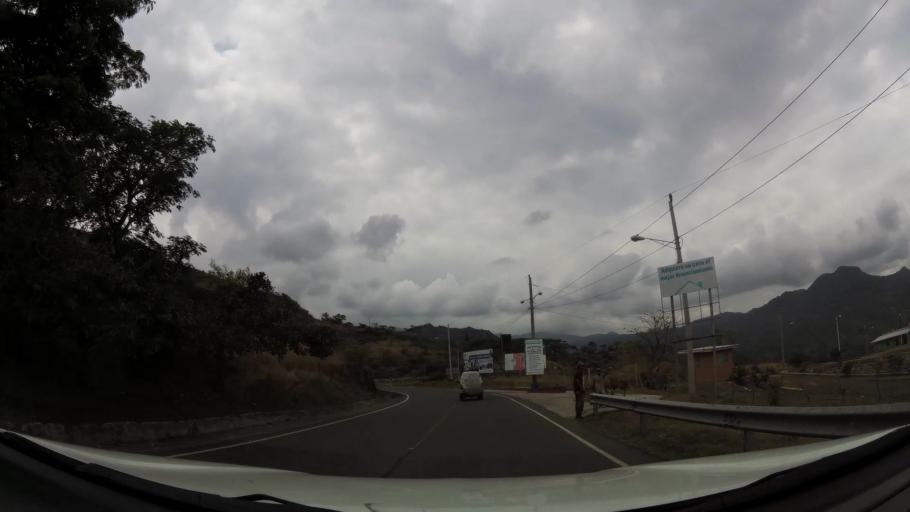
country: NI
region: Matagalpa
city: Matagalpa
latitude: 12.9490
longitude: -85.9203
